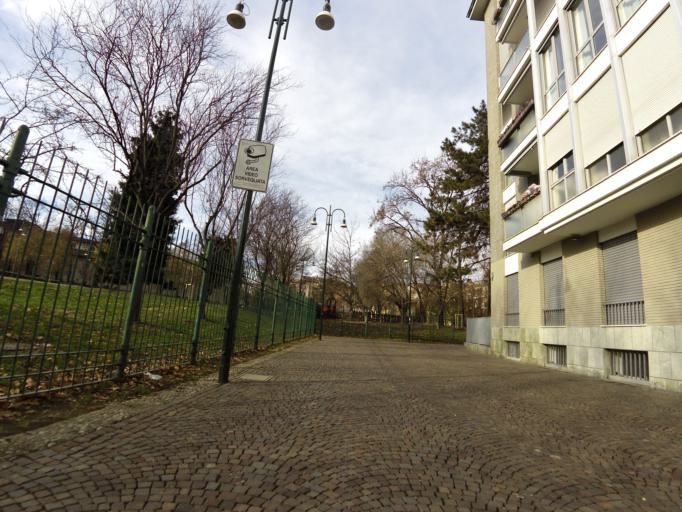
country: IT
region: Lombardy
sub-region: Citta metropolitana di Milano
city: Milano
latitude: 45.4549
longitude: 9.1830
